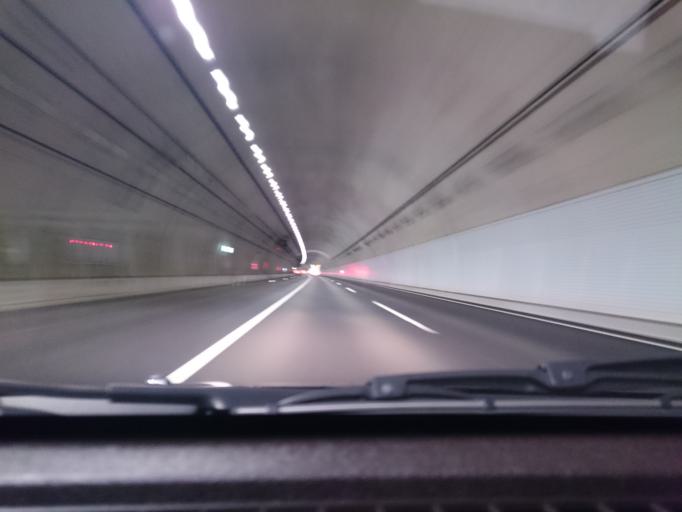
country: JP
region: Shizuoka
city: Hamakita
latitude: 34.8648
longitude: 137.6806
